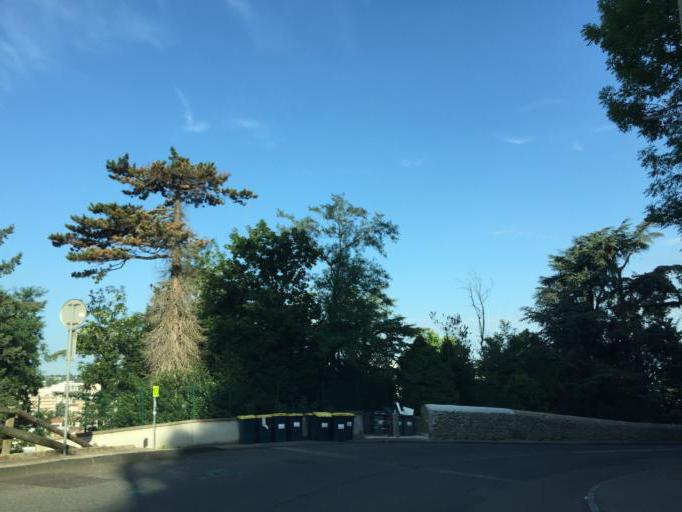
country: FR
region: Rhone-Alpes
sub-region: Departement de la Loire
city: Saint-Etienne
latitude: 45.4170
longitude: 4.4073
